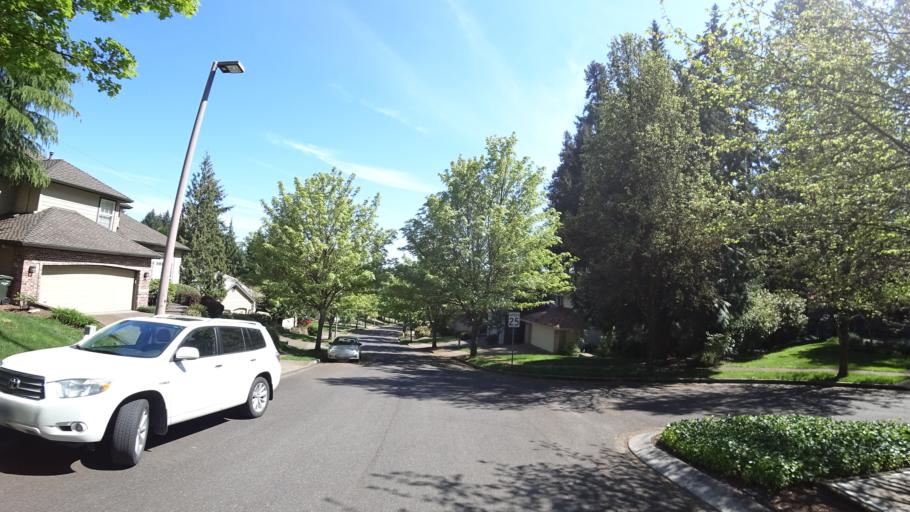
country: US
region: Oregon
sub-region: Washington County
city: Beaverton
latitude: 45.4455
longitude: -122.8403
